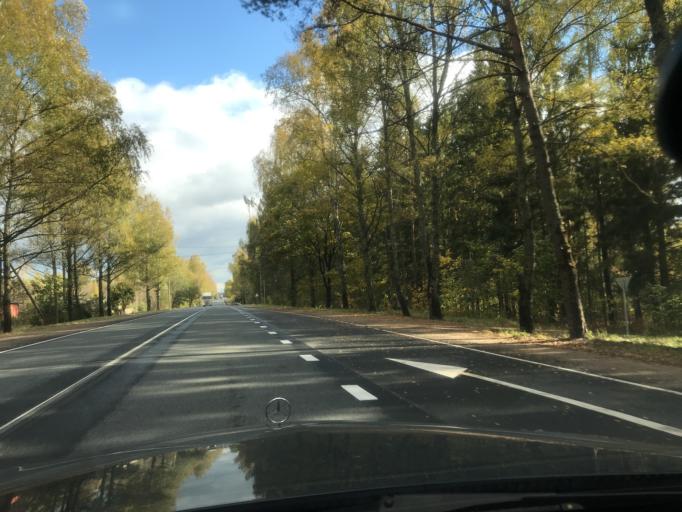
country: RU
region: Pskov
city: Opochka
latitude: 56.6281
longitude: 28.8097
